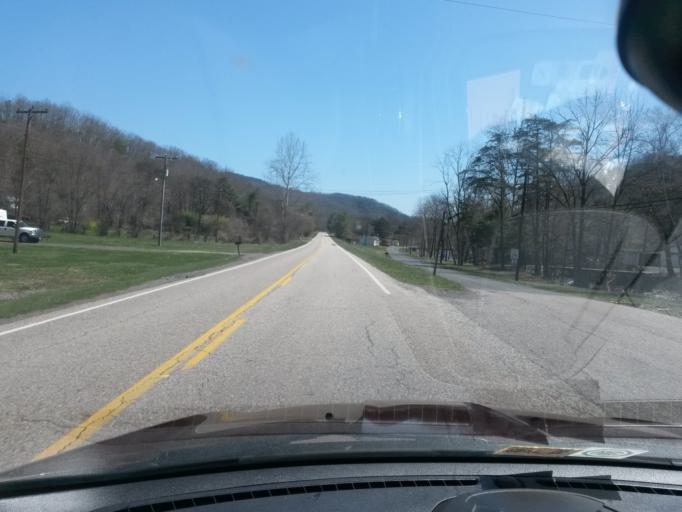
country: US
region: Virginia
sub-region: City of Covington
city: Covington
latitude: 37.8141
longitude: -80.0878
